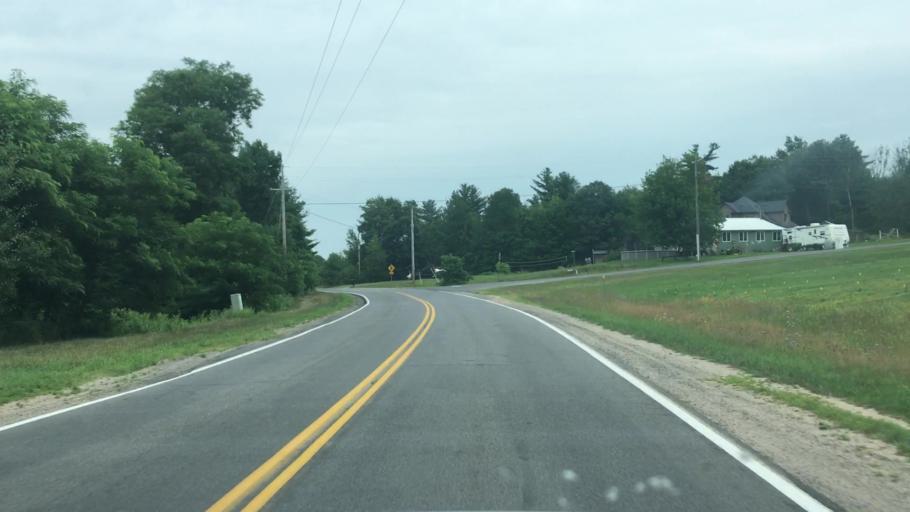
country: US
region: New York
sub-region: Clinton County
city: Morrisonville
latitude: 44.6102
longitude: -73.6311
